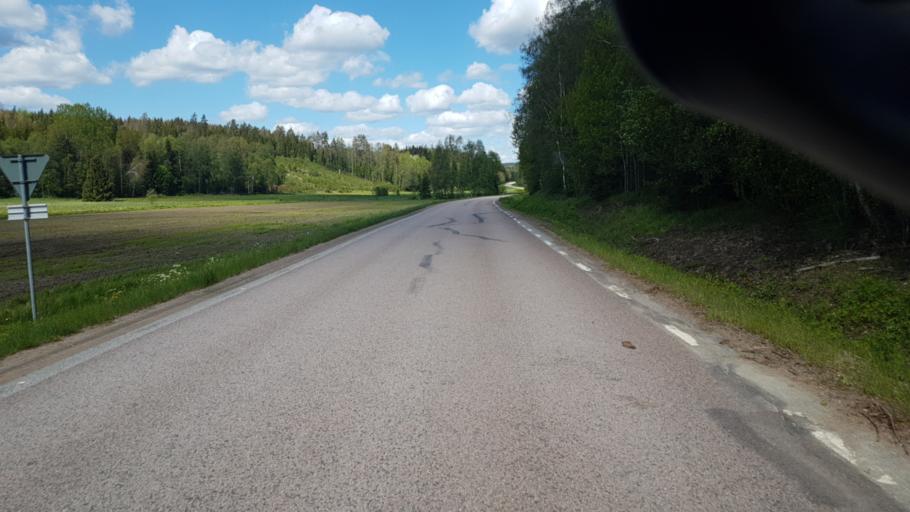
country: SE
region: Vaermland
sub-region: Arvika Kommun
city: Arvika
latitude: 59.6691
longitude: 12.7974
